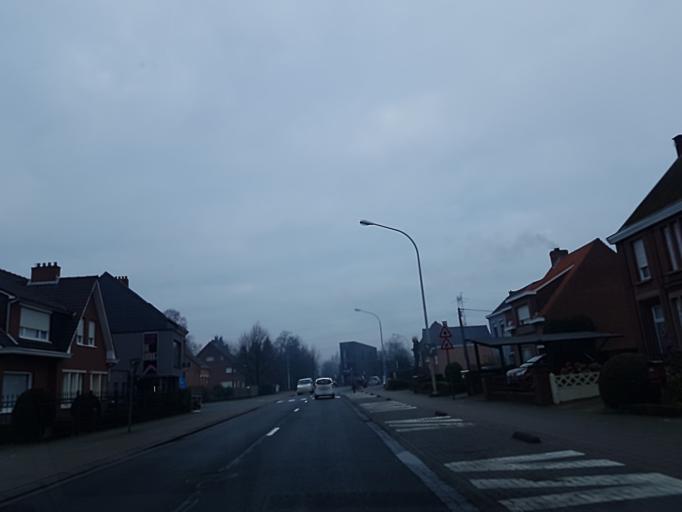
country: BE
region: Flanders
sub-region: Provincie Antwerpen
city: Grobbendonk
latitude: 51.1739
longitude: 4.7427
